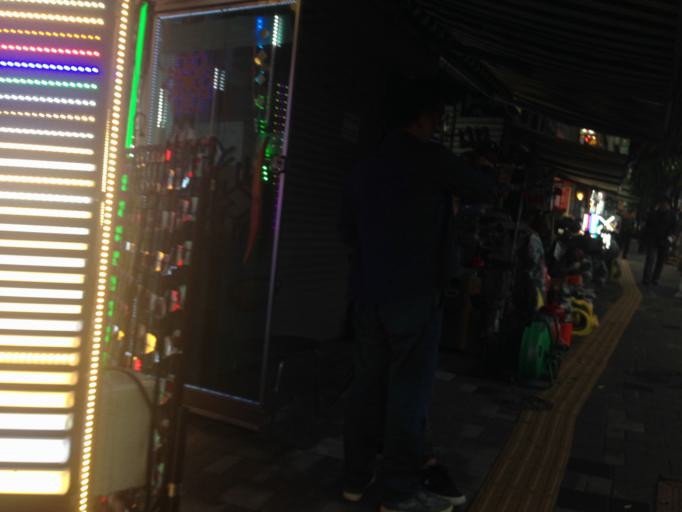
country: KR
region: Seoul
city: Seoul
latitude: 37.5686
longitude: 126.9977
